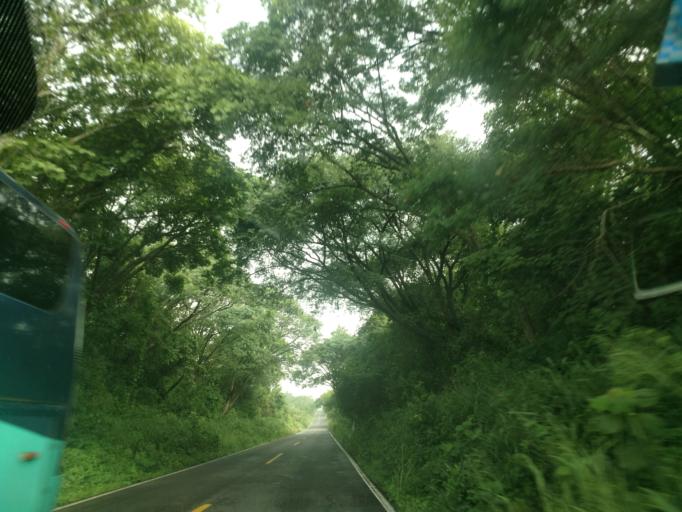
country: MX
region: Jalisco
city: Ameca
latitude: 20.5349
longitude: -104.1369
